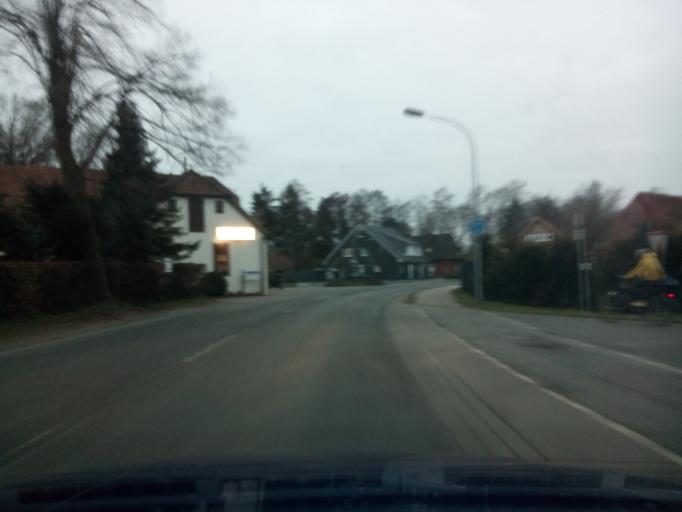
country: DE
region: Lower Saxony
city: Lilienthal
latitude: 53.1530
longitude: 8.9128
